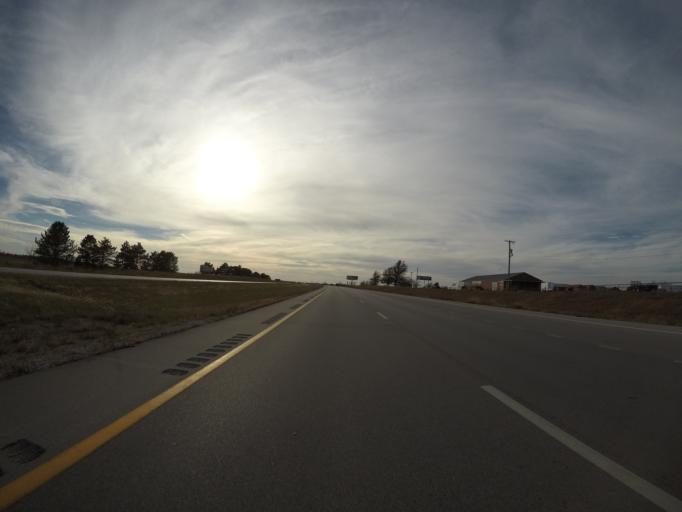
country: US
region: Kansas
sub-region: Johnson County
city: Edgerton
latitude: 38.7450
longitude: -95.0059
